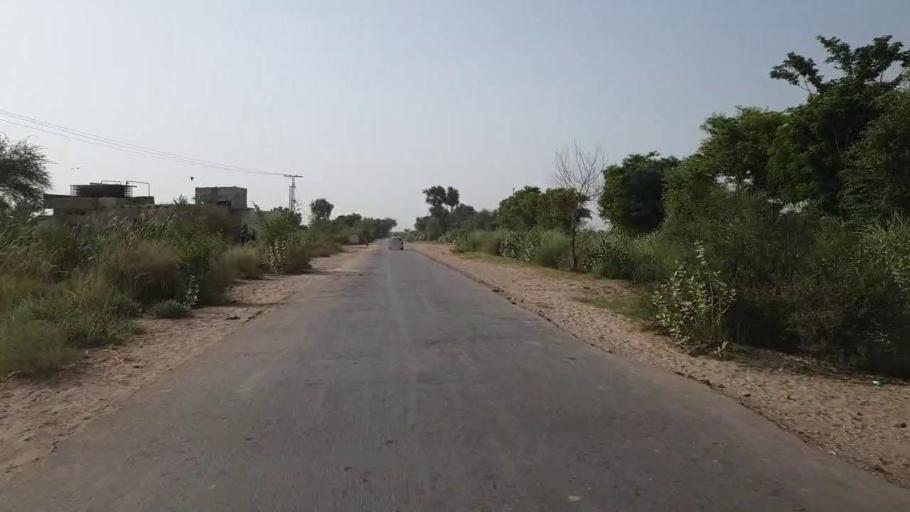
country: PK
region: Sindh
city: Sanghar
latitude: 26.2613
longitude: 68.9312
